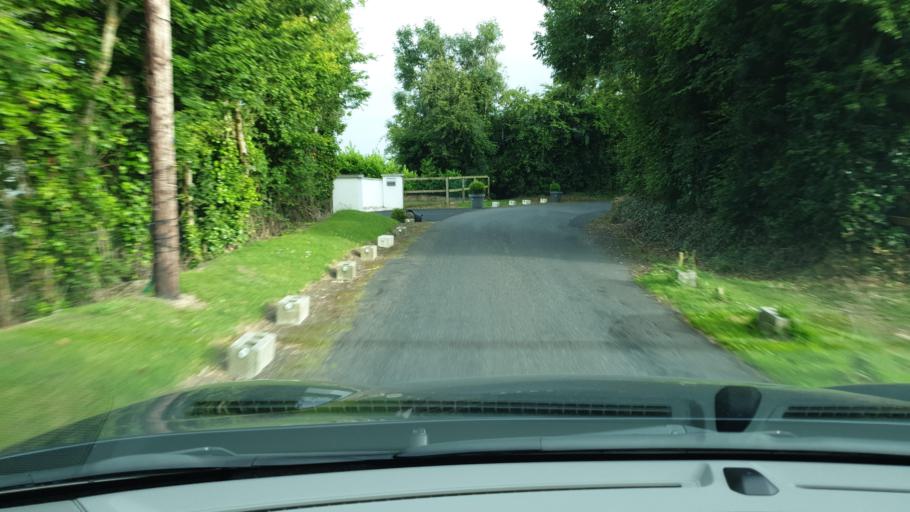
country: IE
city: Confey
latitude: 53.4035
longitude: -6.5088
